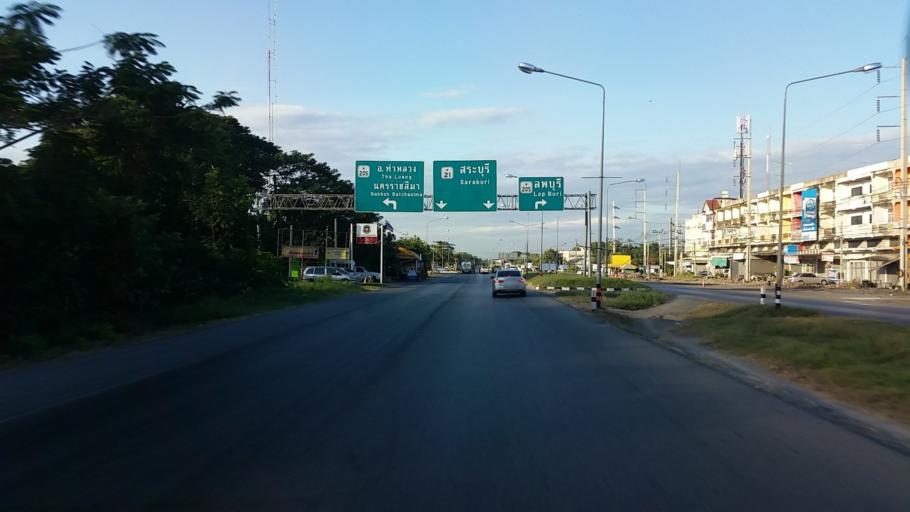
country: TH
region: Lop Buri
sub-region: Amphoe Tha Luang
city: Tha Luang
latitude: 15.0795
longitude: 100.9989
